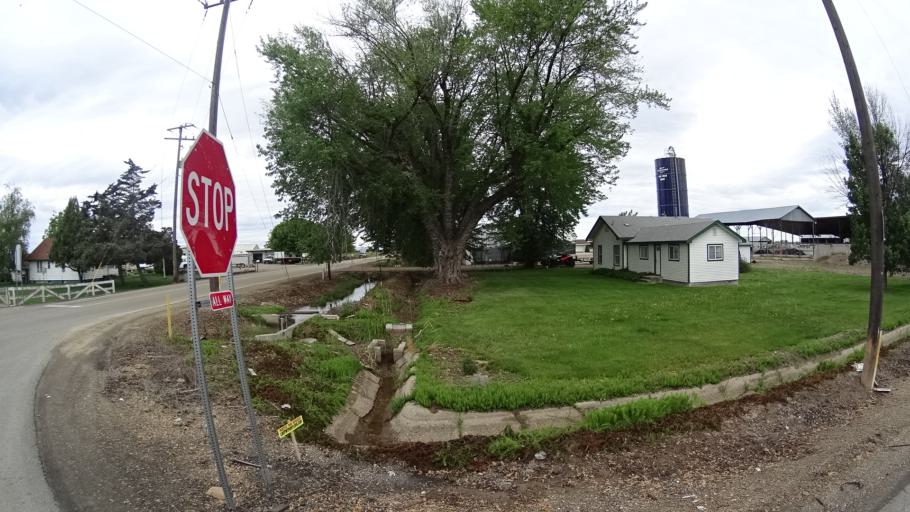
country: US
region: Idaho
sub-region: Ada County
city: Star
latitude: 43.6343
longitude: -116.4936
